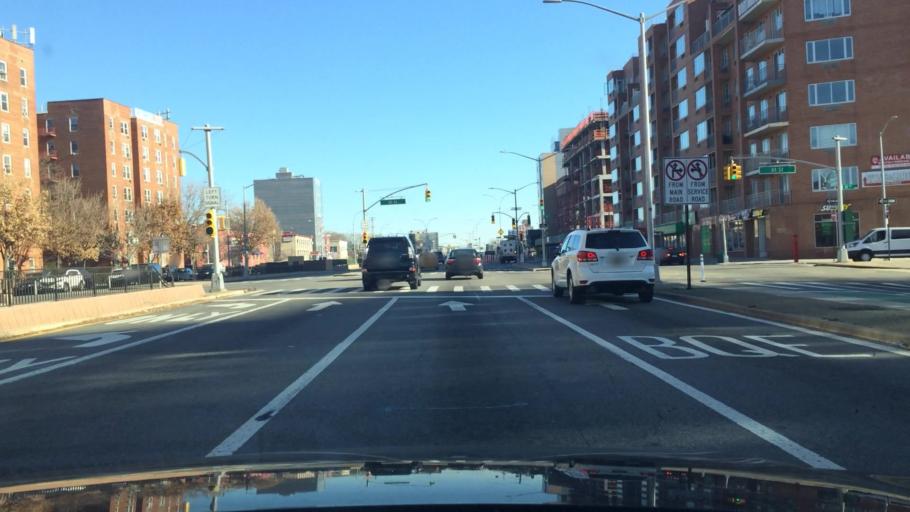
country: US
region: New York
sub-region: Queens County
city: Long Island City
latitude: 40.7413
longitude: -73.9031
